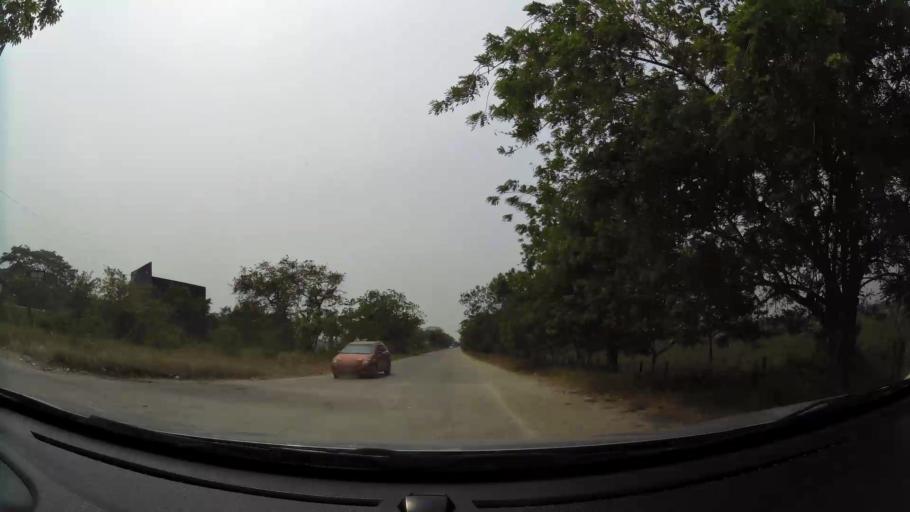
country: HN
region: Cortes
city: La Lima
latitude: 15.4212
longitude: -87.8953
